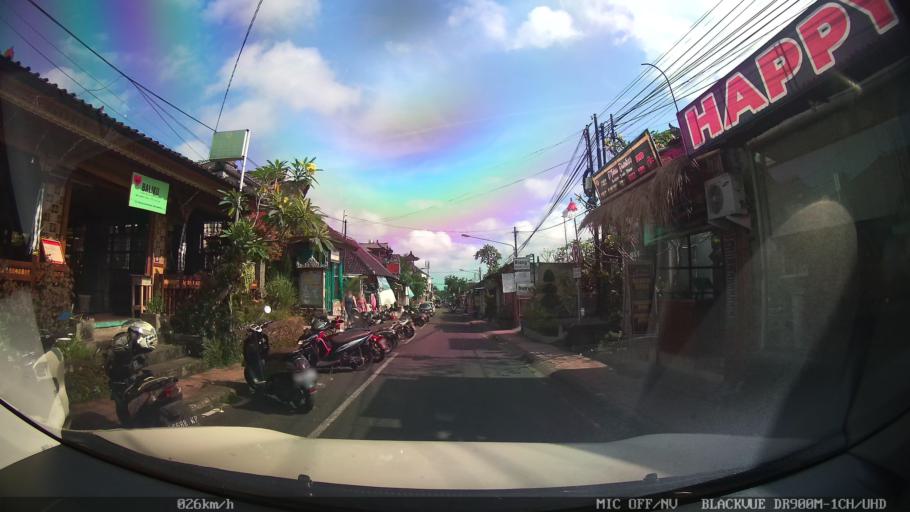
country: ID
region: Bali
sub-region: Kabupaten Gianyar
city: Ubud
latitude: -8.5122
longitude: 115.2683
